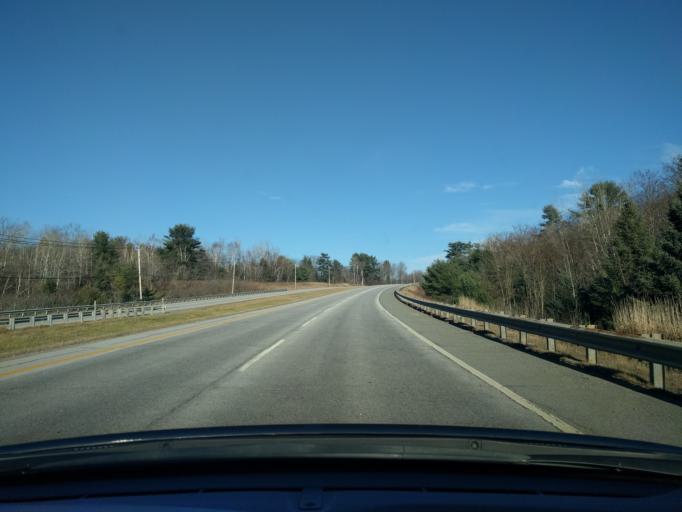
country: US
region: Maine
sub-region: Penobscot County
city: Hampden
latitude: 44.7503
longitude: -68.8446
